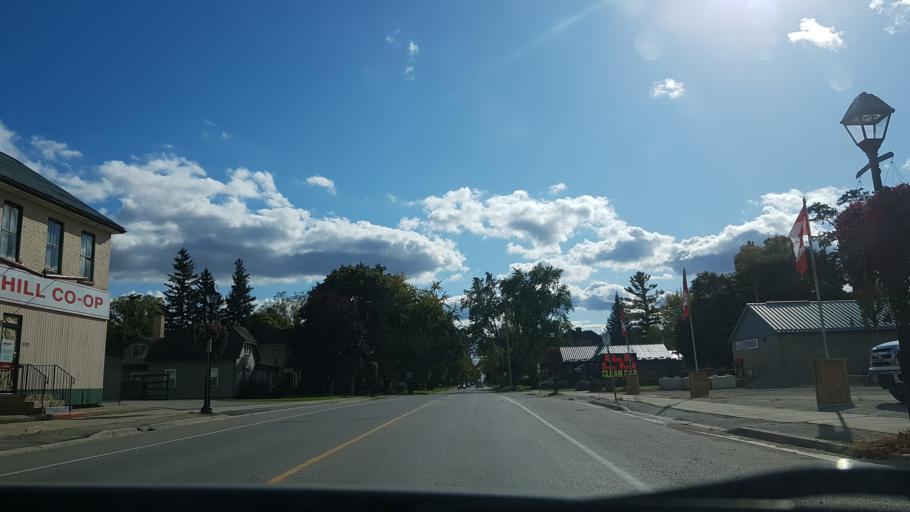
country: CA
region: Ontario
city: South Huron
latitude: 43.1618
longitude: -81.6844
